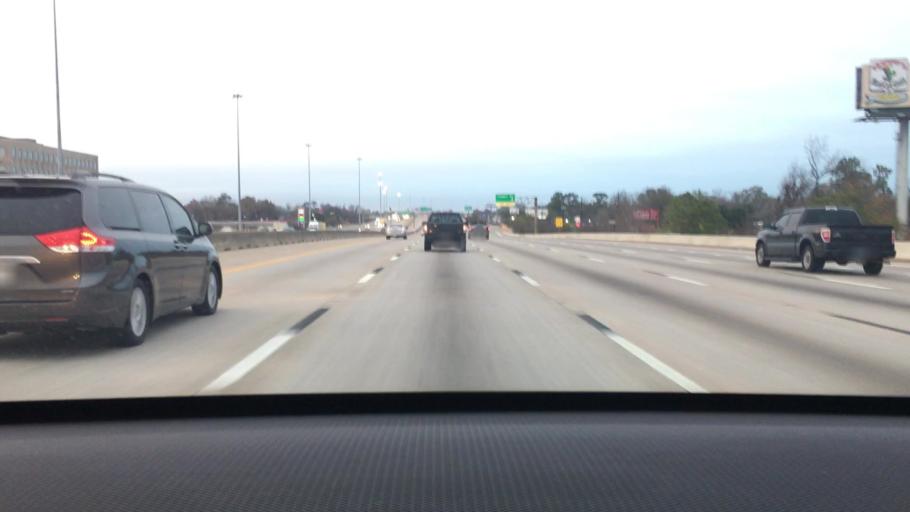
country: US
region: Texas
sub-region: Harris County
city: Houston
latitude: 29.8412
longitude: -95.3334
